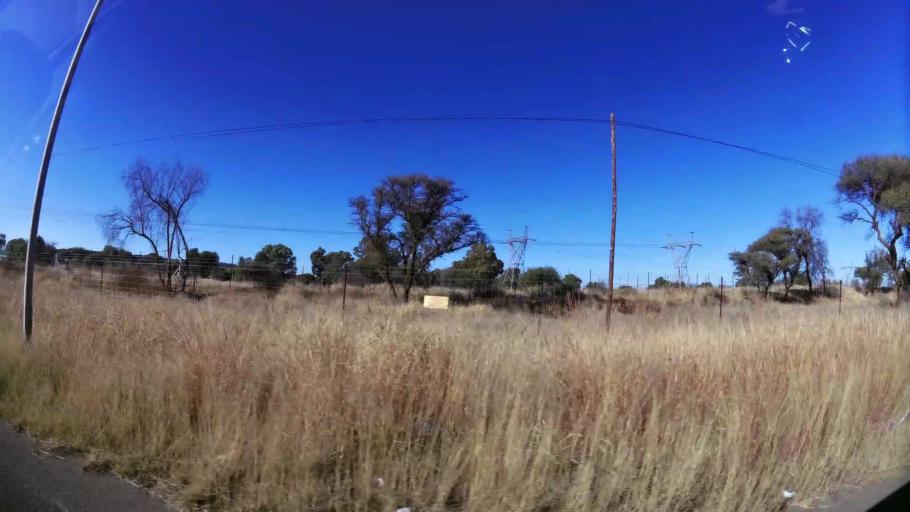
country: ZA
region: Northern Cape
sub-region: Frances Baard District Municipality
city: Kimberley
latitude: -28.7478
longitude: 24.7948
